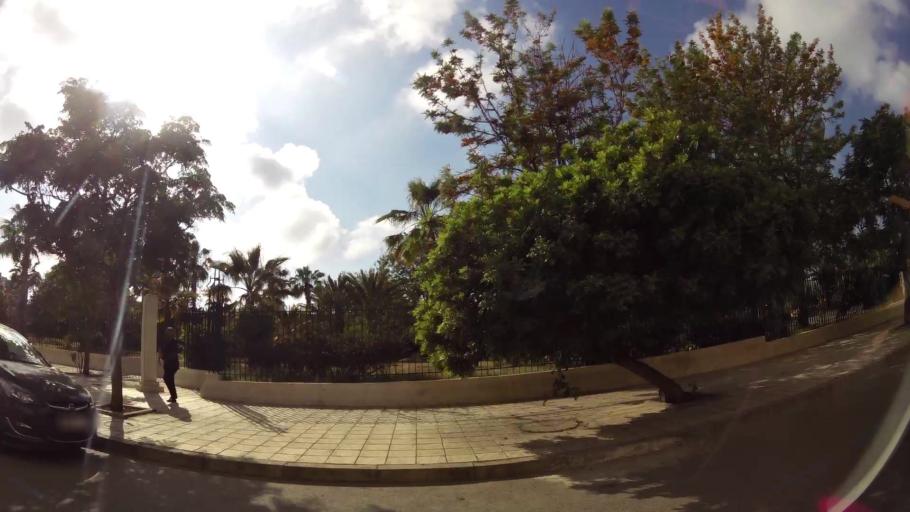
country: MA
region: Rabat-Sale-Zemmour-Zaer
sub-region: Skhirate-Temara
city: Temara
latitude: 33.9562
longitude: -6.8710
